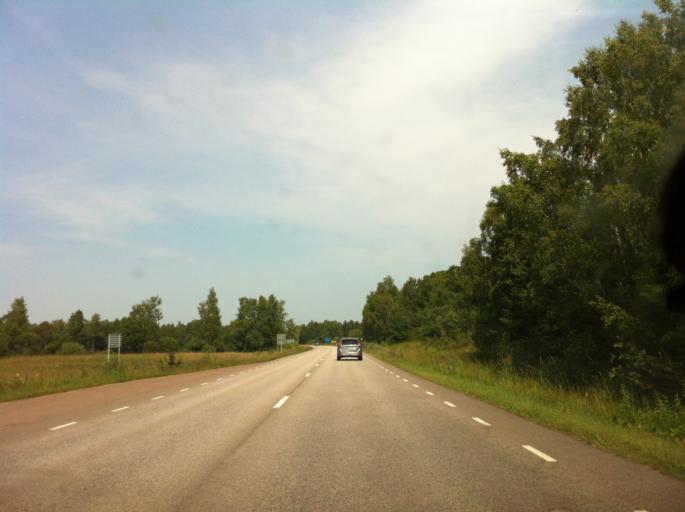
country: SE
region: Kalmar
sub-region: Borgholms Kommun
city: Borgholm
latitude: 57.0182
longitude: 16.8531
